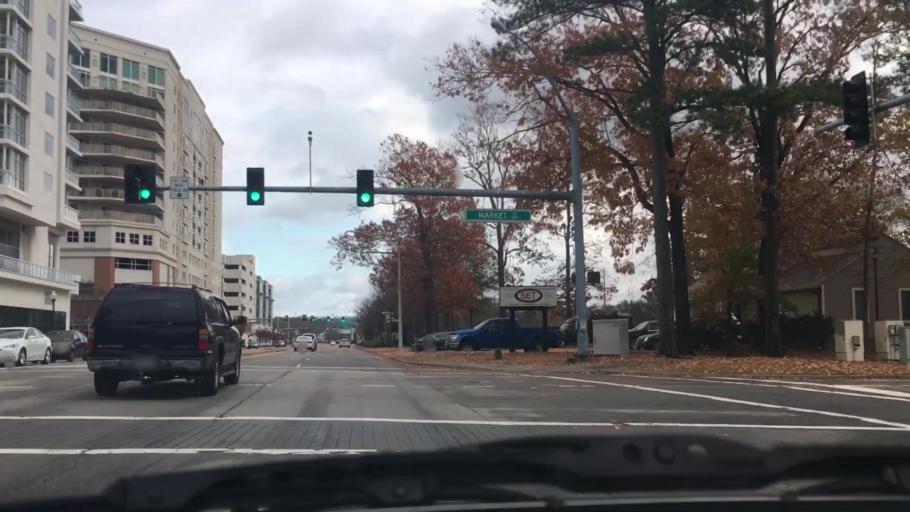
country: US
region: Virginia
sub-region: City of Chesapeake
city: Chesapeake
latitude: 36.8409
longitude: -76.1350
